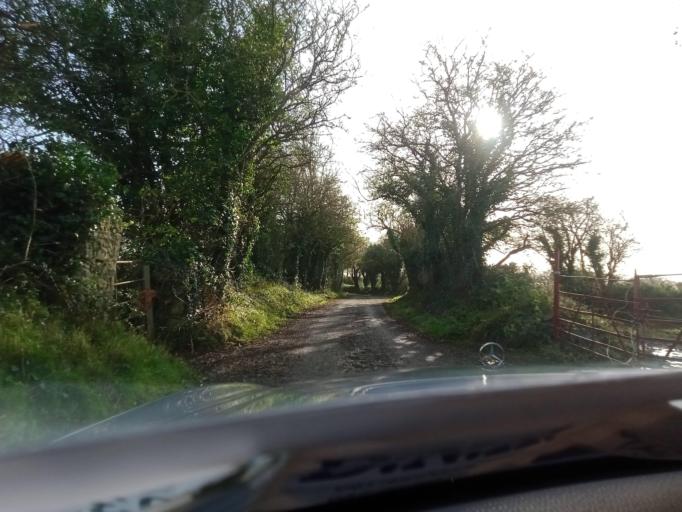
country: IE
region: Leinster
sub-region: Kilkenny
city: Mooncoin
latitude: 52.3186
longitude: -7.2830
